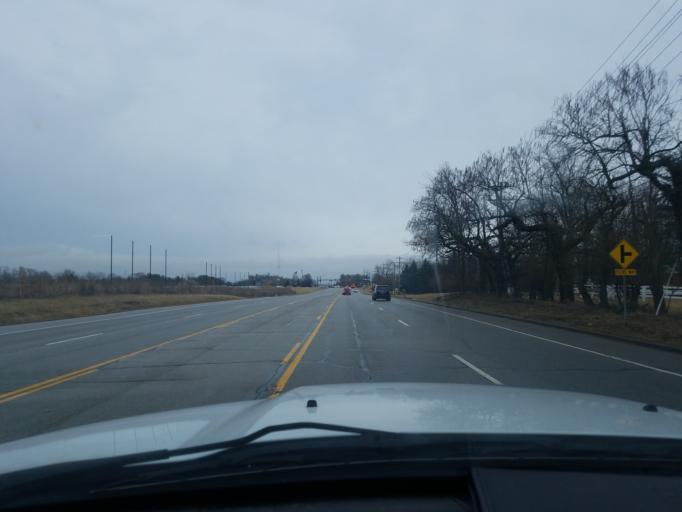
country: US
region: Ohio
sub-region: Butler County
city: Wetherington
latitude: 39.3522
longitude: -84.3527
